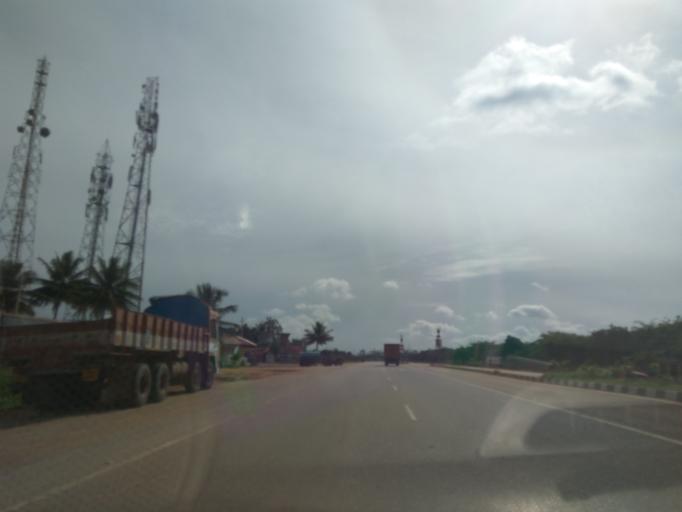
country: IN
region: Karnataka
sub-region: Bangalore Rural
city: Dasarahalli
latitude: 13.0898
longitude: 77.8355
